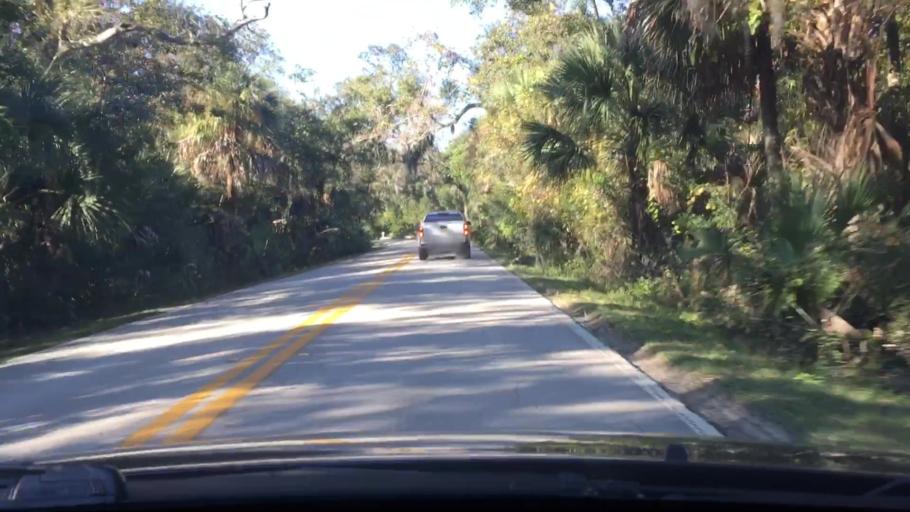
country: US
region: Florida
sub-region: Volusia County
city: Ormond-by-the-Sea
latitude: 29.3409
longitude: -81.0840
